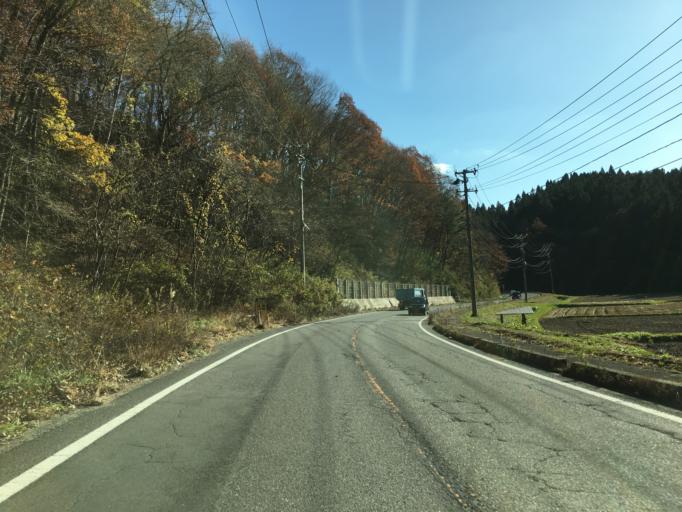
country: JP
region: Fukushima
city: Funehikimachi-funehiki
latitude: 37.2627
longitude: 140.6309
